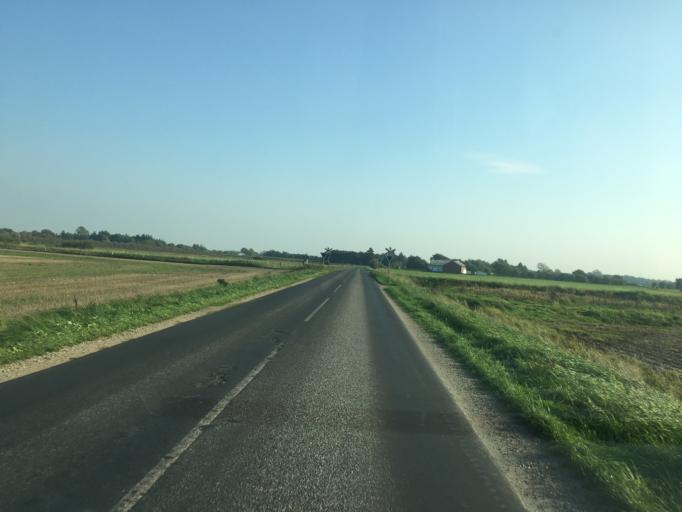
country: DE
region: Schleswig-Holstein
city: Bramstedtlund
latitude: 54.9434
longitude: 9.0635
